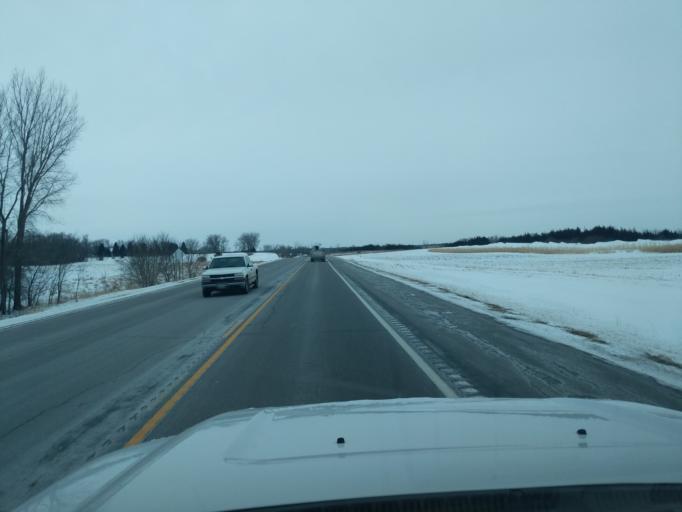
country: US
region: Minnesota
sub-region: Redwood County
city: Redwood Falls
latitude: 44.5645
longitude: -94.9967
